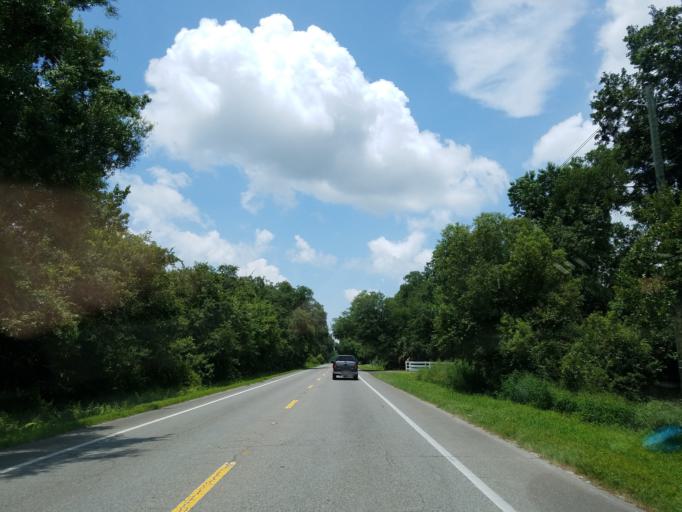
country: US
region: Florida
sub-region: Hillsborough County
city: Fish Hawk
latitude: 27.8506
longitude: -82.1077
